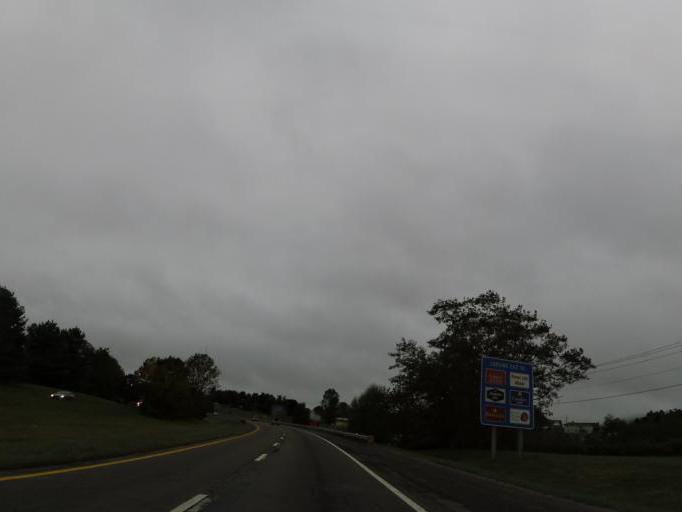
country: US
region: Virginia
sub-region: Wythe County
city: Wytheville
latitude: 36.9653
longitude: -81.0748
